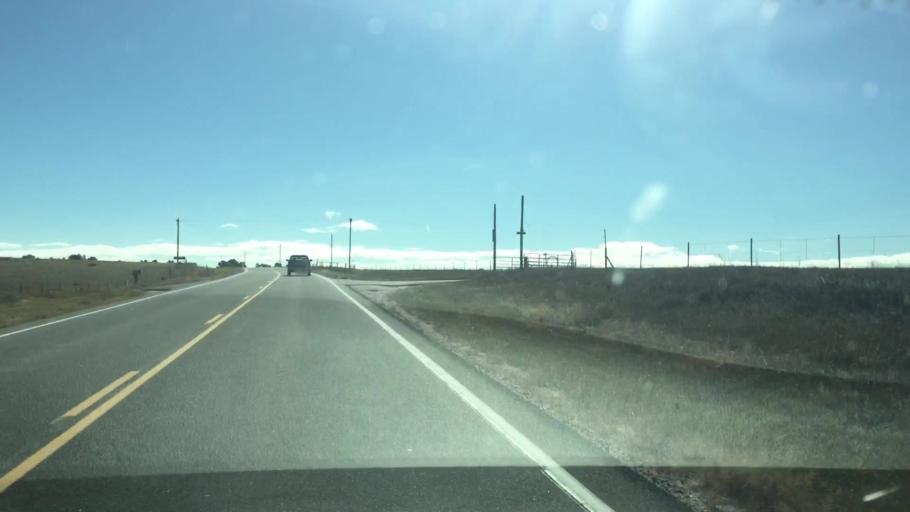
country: US
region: Colorado
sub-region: Elbert County
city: Kiowa
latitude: 39.3336
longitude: -104.4199
